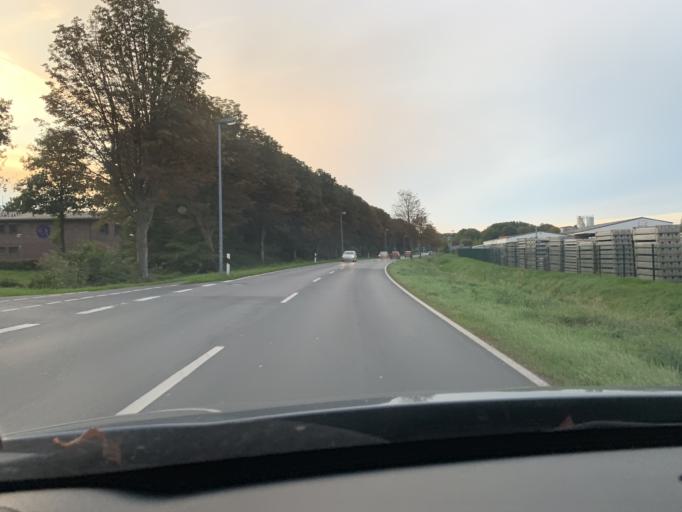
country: DE
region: Lower Saxony
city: Westerstede
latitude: 53.2498
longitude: 7.9199
